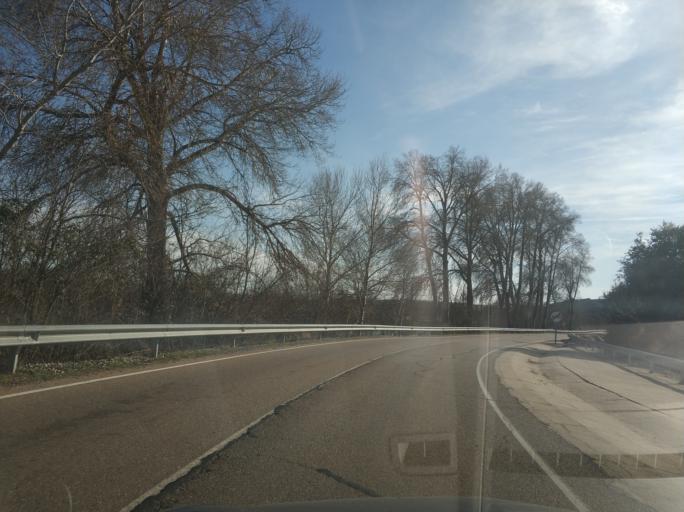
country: ES
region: Castille and Leon
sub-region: Provincia de Salamanca
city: Carrascal de Barregas
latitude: 40.9987
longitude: -5.7323
